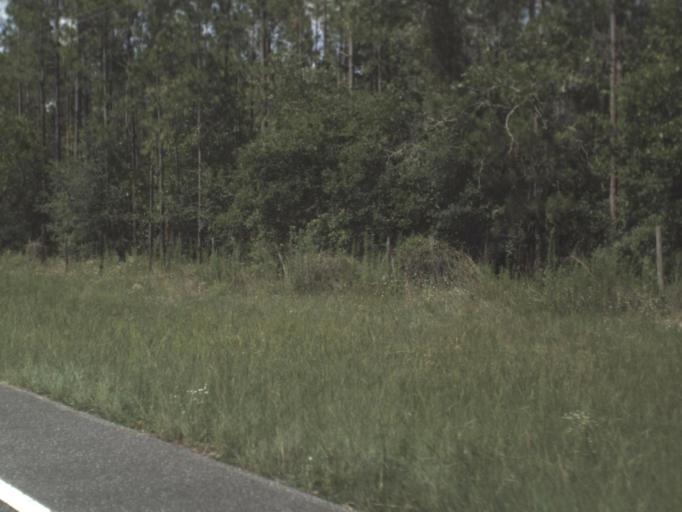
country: US
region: Florida
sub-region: Alachua County
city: High Springs
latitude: 29.8008
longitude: -82.7411
